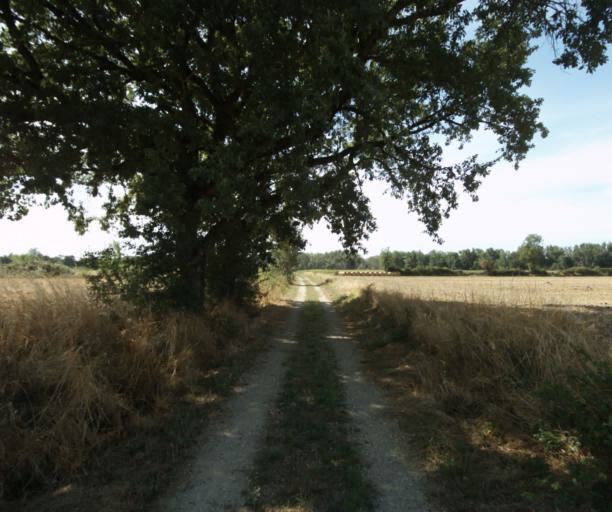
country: FR
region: Midi-Pyrenees
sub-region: Departement du Tarn
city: Soual
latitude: 43.5231
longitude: 2.0764
